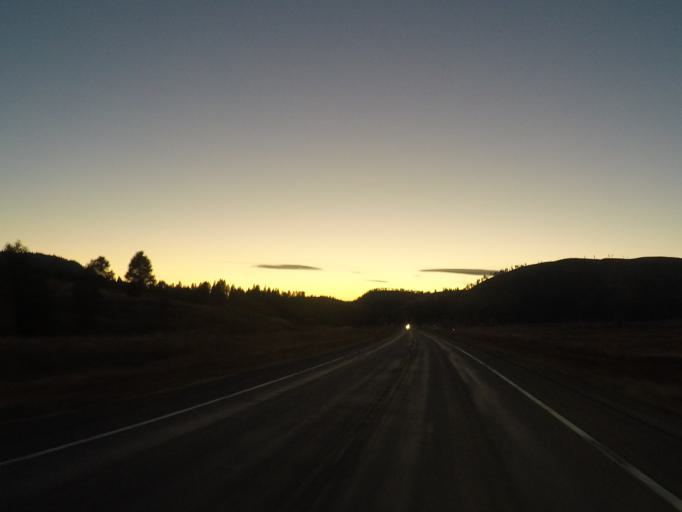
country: US
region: Montana
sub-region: Missoula County
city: Seeley Lake
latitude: 47.0309
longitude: -113.2562
